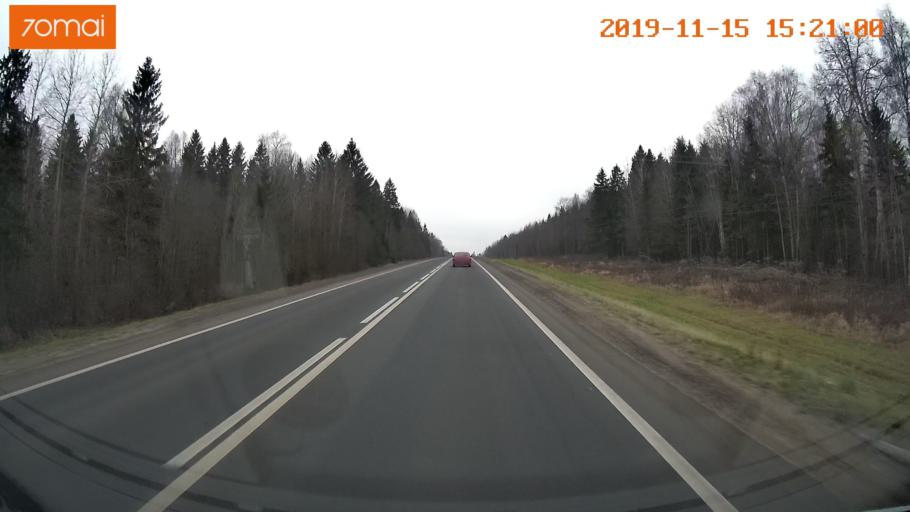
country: RU
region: Jaroslavl
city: Danilov
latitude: 58.2174
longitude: 40.1527
